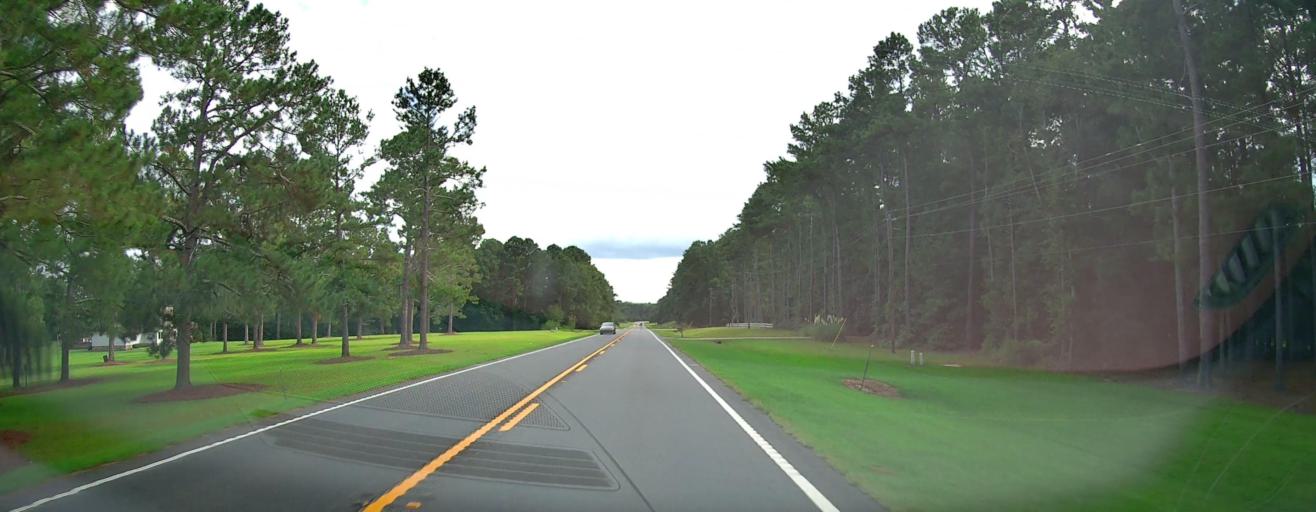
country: US
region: Georgia
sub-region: Meriwether County
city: Manchester
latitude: 32.9732
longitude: -84.5999
